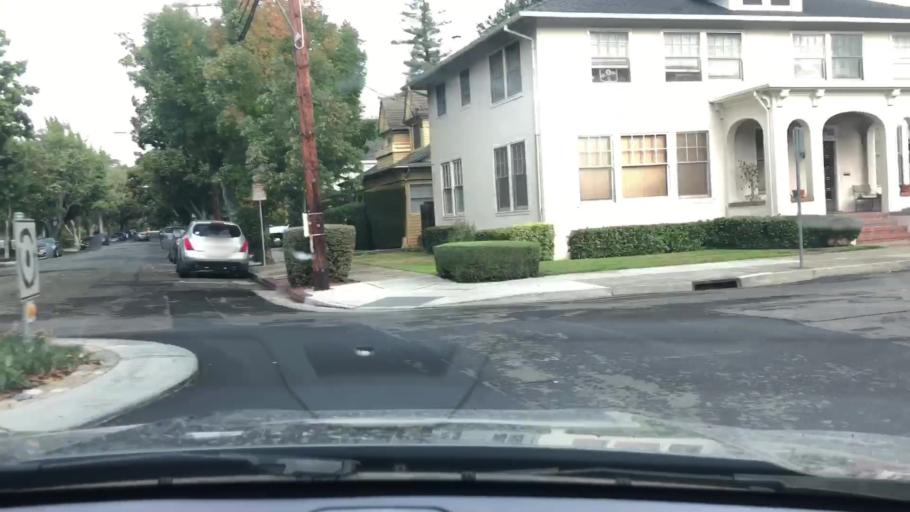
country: US
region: California
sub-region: San Mateo County
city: Menlo Park
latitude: 37.4463
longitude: -122.1653
